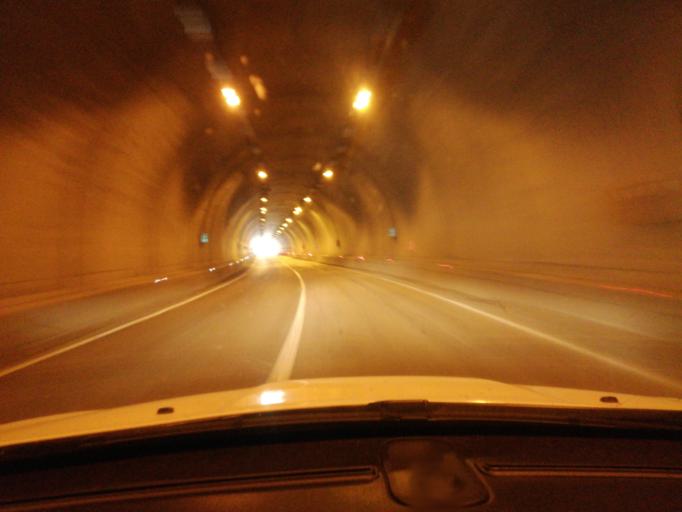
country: TR
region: Karabuk
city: Yenice
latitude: 41.1614
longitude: 32.4580
